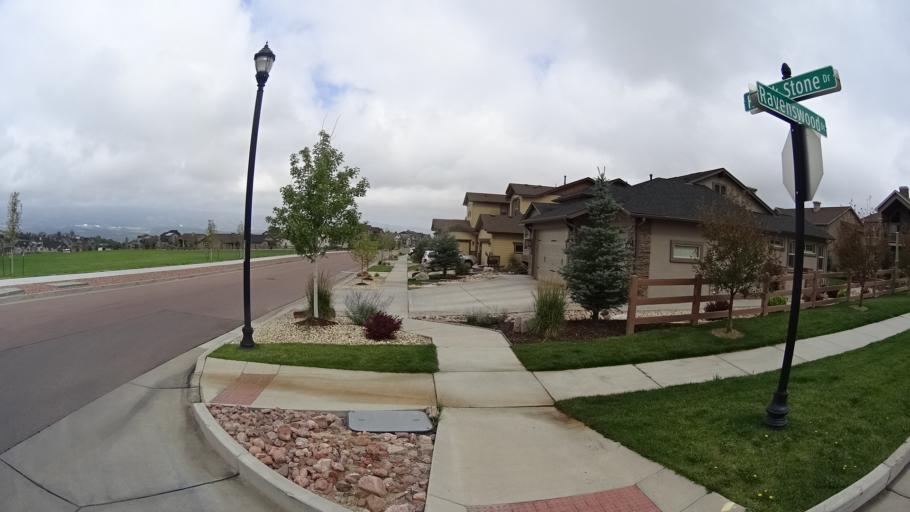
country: US
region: Colorado
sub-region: El Paso County
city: Gleneagle
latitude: 39.0109
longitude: -104.7884
